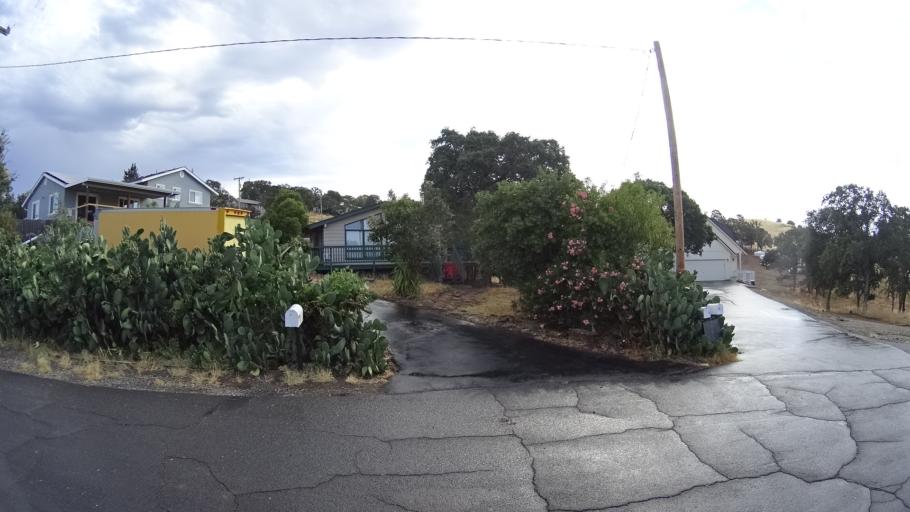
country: US
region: California
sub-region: Calaveras County
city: Copperopolis
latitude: 37.9078
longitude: -120.6135
